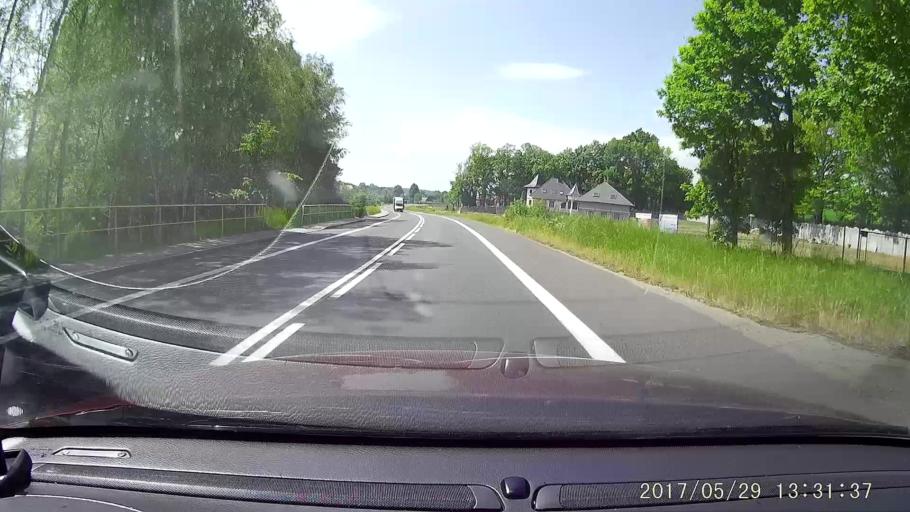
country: PL
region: Lower Silesian Voivodeship
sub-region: Powiat lubanski
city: Olszyna
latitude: 51.0808
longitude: 15.3394
